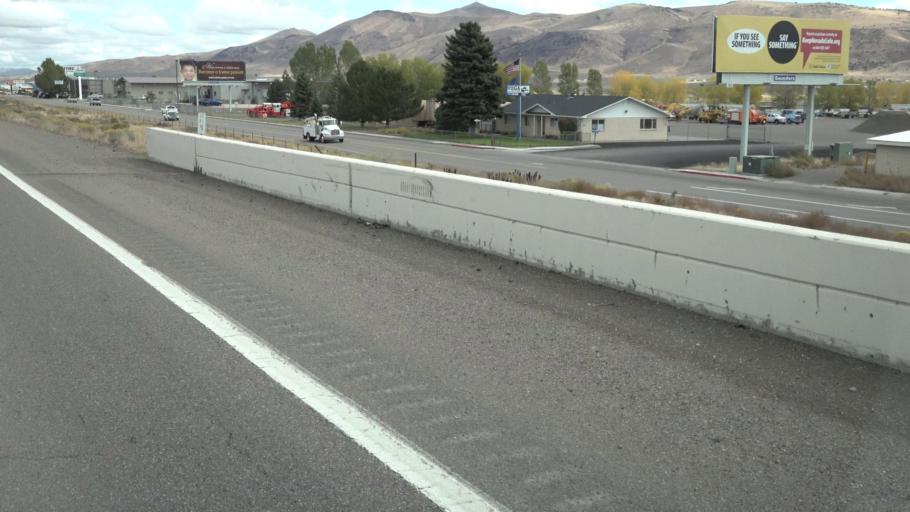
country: US
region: Nevada
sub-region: Elko County
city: Elko
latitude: 40.8648
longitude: -115.7337
